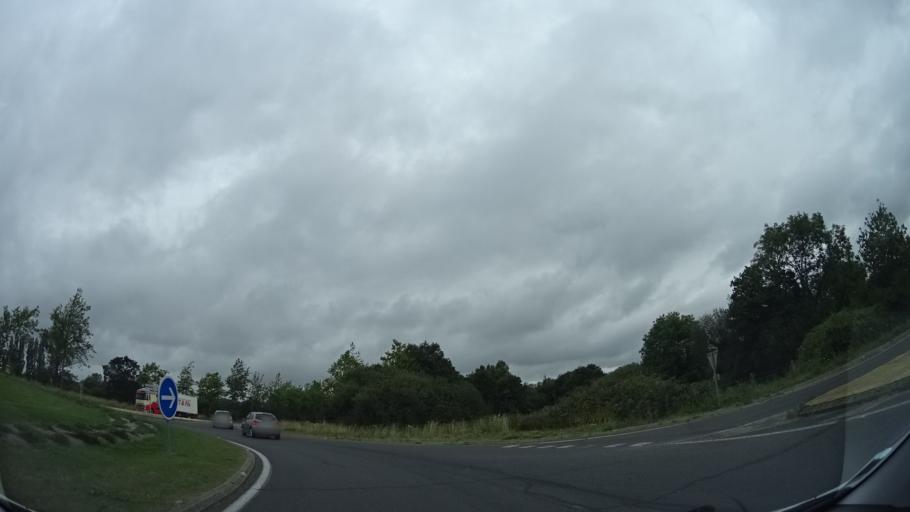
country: FR
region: Lower Normandy
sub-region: Departement de la Manche
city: La Haye-du-Puits
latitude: 49.2949
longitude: -1.5577
